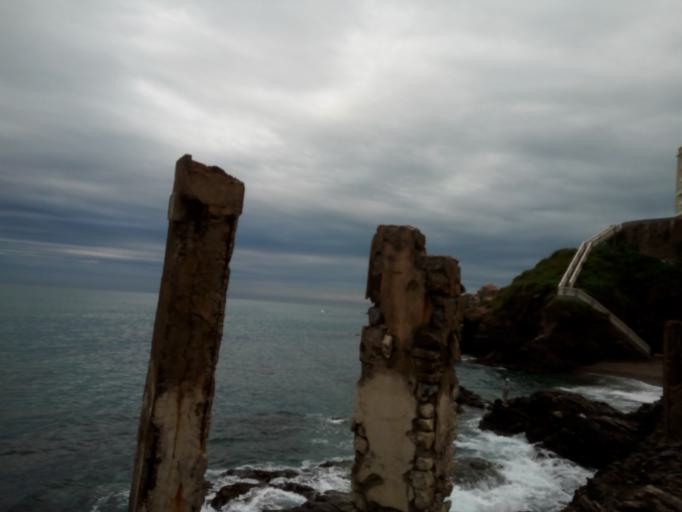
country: DZ
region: Alger
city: Algiers
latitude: 36.8124
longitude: 3.0229
